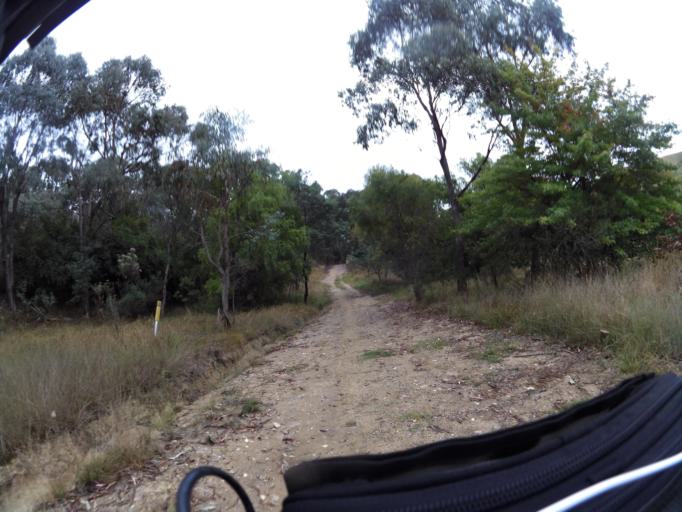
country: AU
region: New South Wales
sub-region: Greater Hume Shire
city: Holbrook
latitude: -36.1551
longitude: 147.4124
